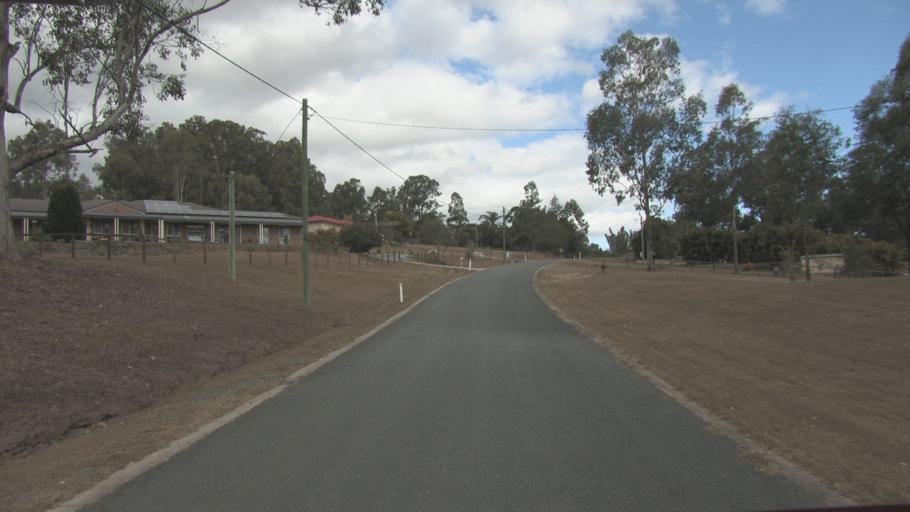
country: AU
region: Queensland
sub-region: Logan
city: Cedar Vale
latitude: -27.8843
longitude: 153.0136
